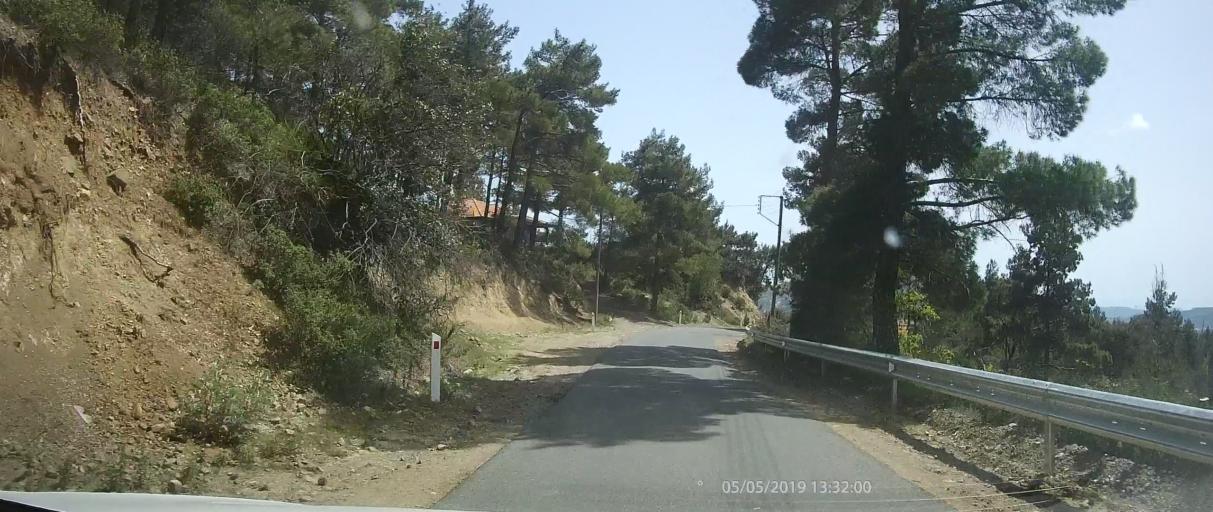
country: CY
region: Lefkosia
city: Kakopetria
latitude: 34.8908
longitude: 32.8517
